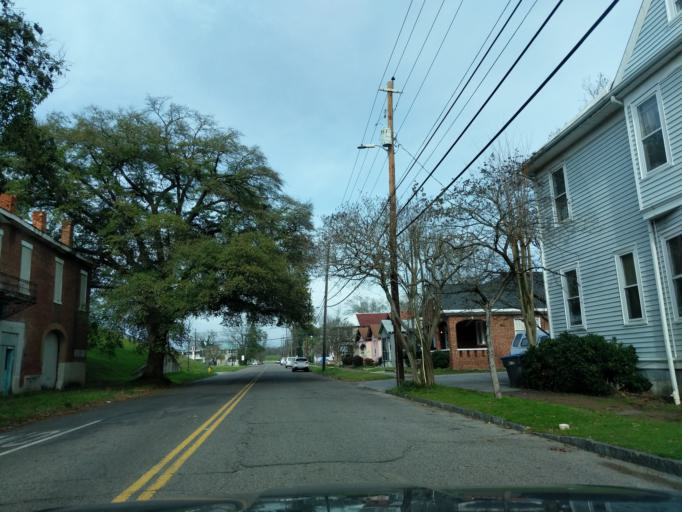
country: US
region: Georgia
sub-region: Richmond County
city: Augusta
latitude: 33.4704
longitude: -81.9570
